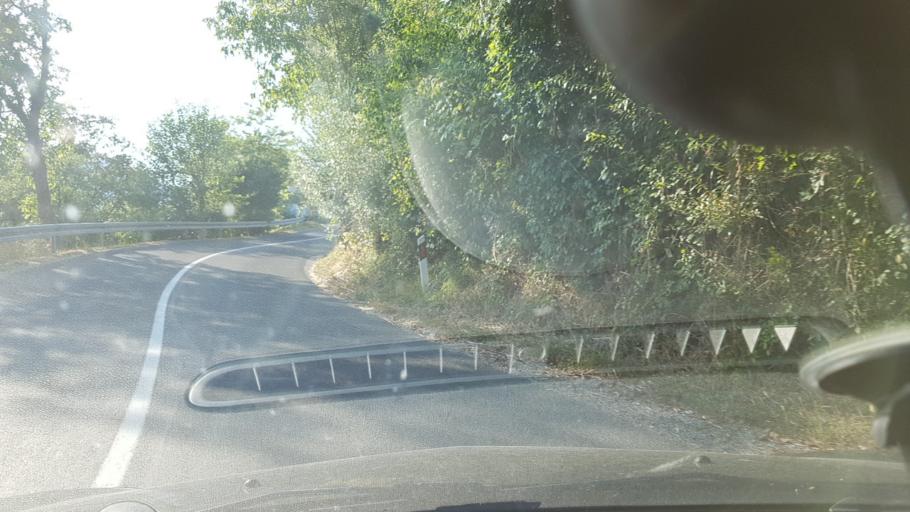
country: SI
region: Bistrica ob Sotli
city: Bistrica ob Sotli
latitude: 46.0477
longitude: 15.7374
